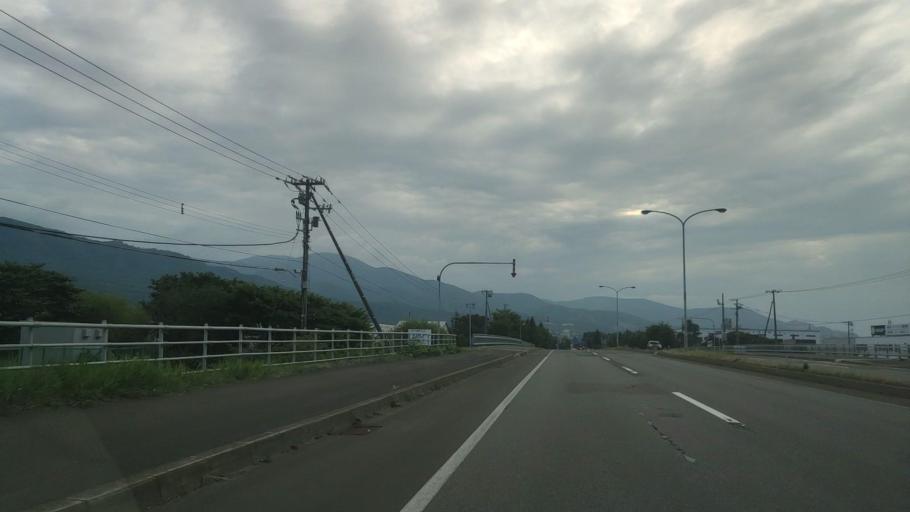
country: JP
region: Hokkaido
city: Sapporo
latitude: 43.1443
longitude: 141.1891
